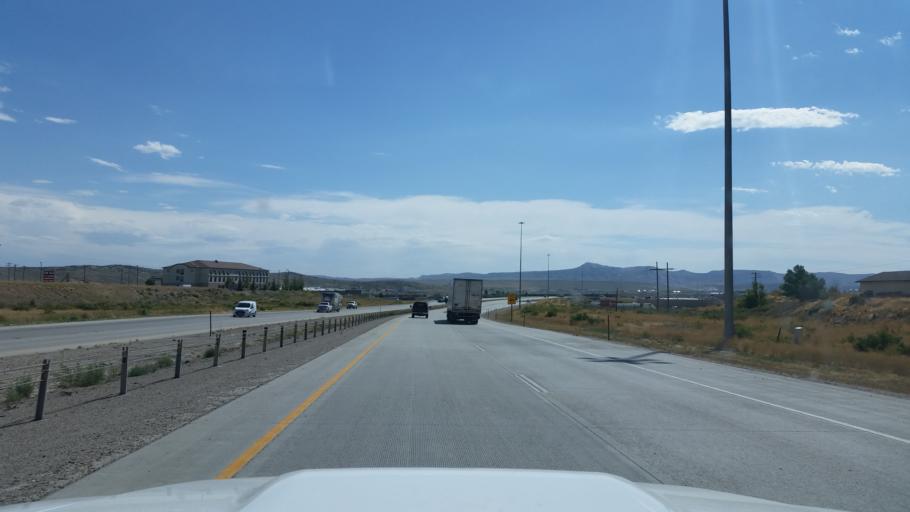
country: US
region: Wyoming
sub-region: Sweetwater County
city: Rock Springs
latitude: 41.5856
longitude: -109.2499
